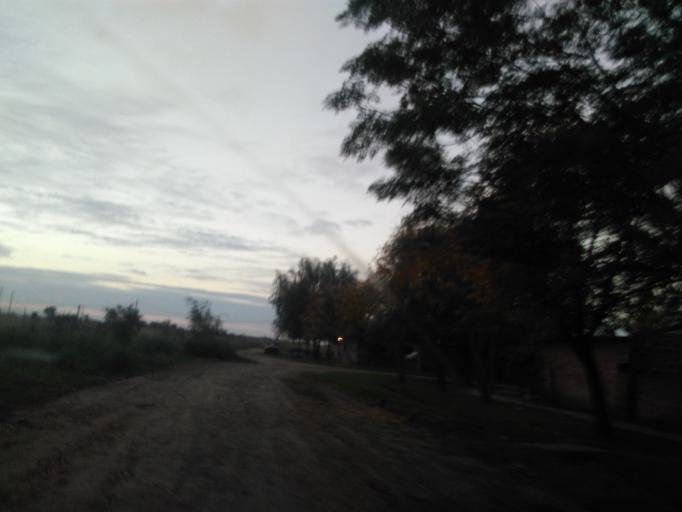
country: AR
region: Chaco
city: Fontana
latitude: -27.3966
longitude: -58.9937
